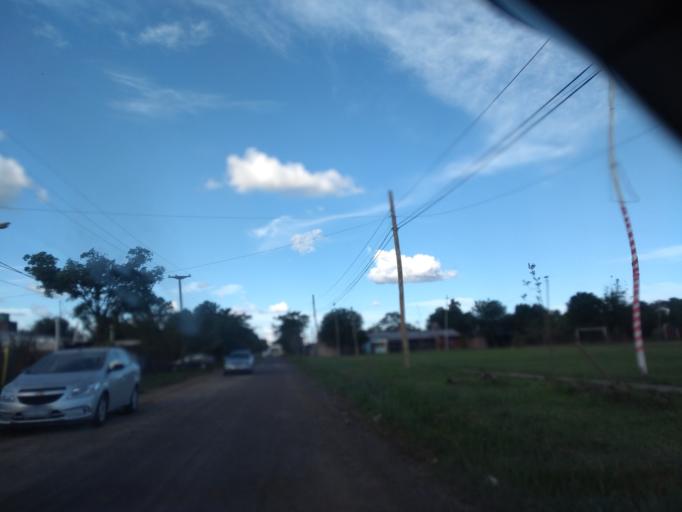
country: AR
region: Chaco
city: Fontana
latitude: -27.4128
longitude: -59.0407
